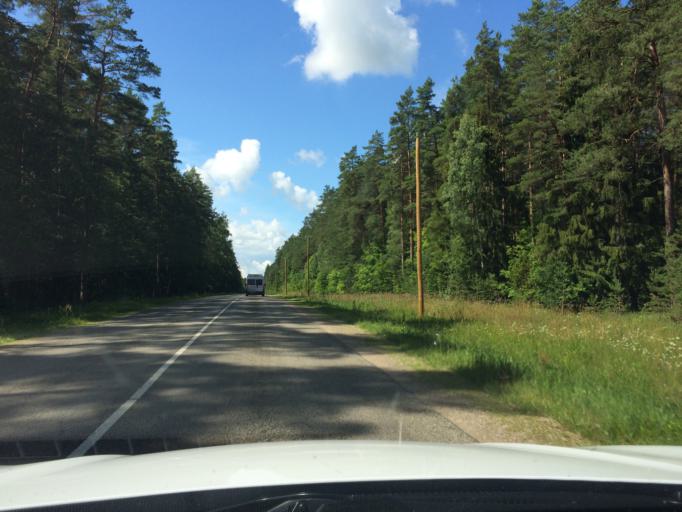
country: LV
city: Tervete
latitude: 56.4840
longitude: 23.4139
